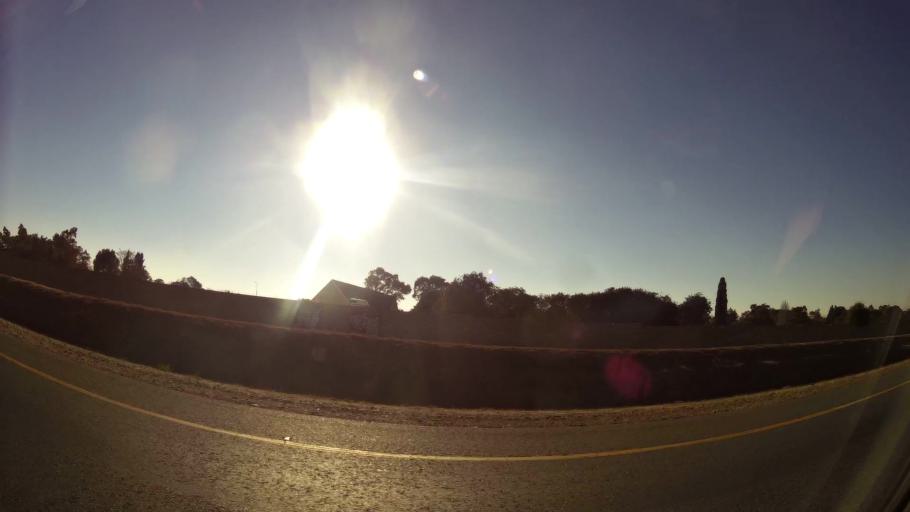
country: ZA
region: Gauteng
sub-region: Ekurhuleni Metropolitan Municipality
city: Germiston
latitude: -26.3012
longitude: 28.1100
